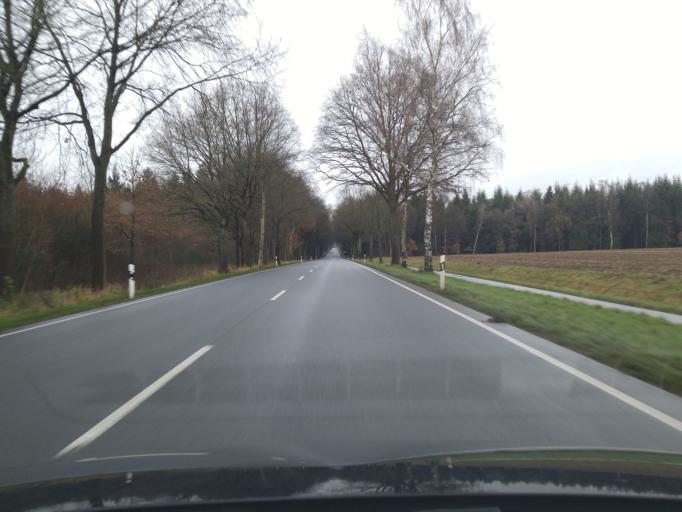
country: DE
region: Lower Saxony
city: Sprakensehl
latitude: 52.7753
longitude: 10.4925
